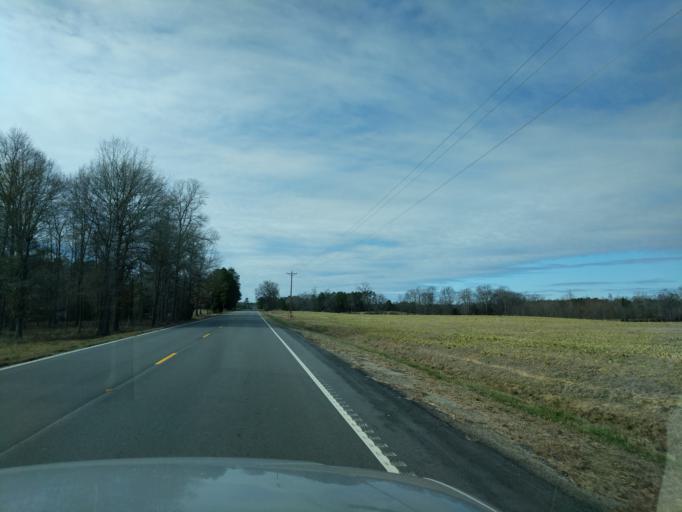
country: US
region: South Carolina
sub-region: Edgefield County
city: Edgefield
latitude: 33.9365
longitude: -81.9541
